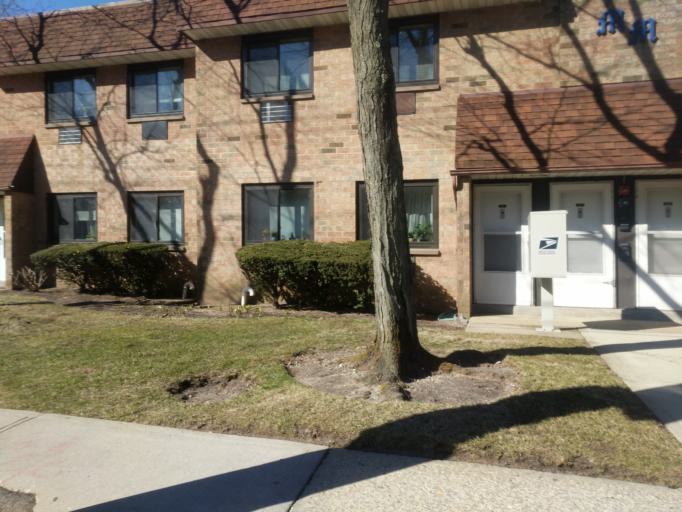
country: US
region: New York
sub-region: Nassau County
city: Inwood
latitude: 40.6132
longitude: -73.7457
